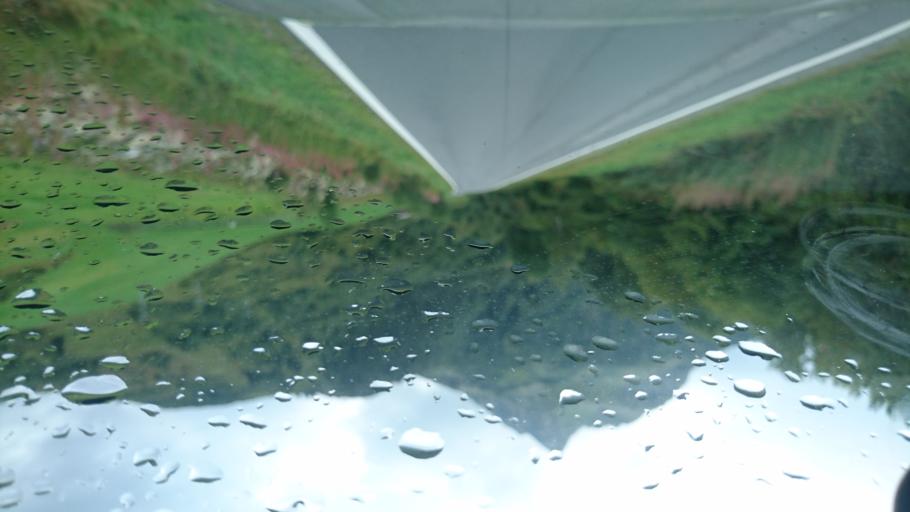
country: AT
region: Tyrol
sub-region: Politischer Bezirk Landeck
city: Galtur
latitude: 46.9633
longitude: 10.1595
